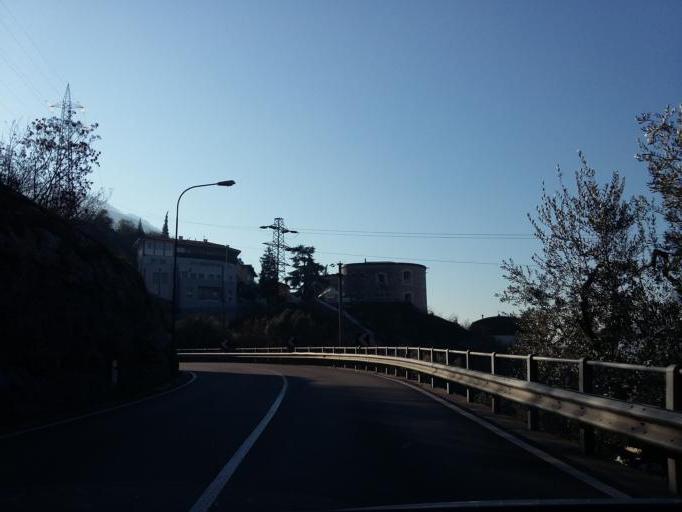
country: IT
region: Trentino-Alto Adige
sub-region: Provincia di Trento
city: Nago-Torbole
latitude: 45.8793
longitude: 10.8877
